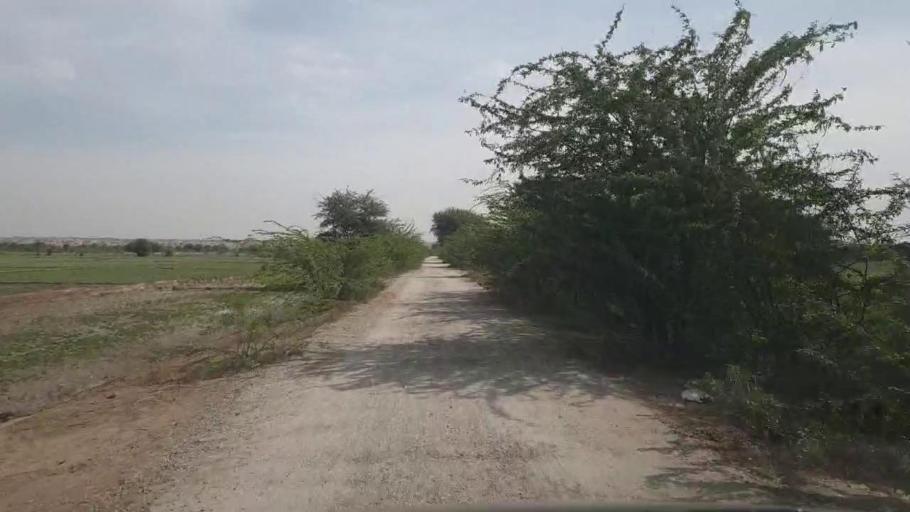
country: PK
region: Sindh
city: Kunri
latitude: 25.1926
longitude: 69.6941
